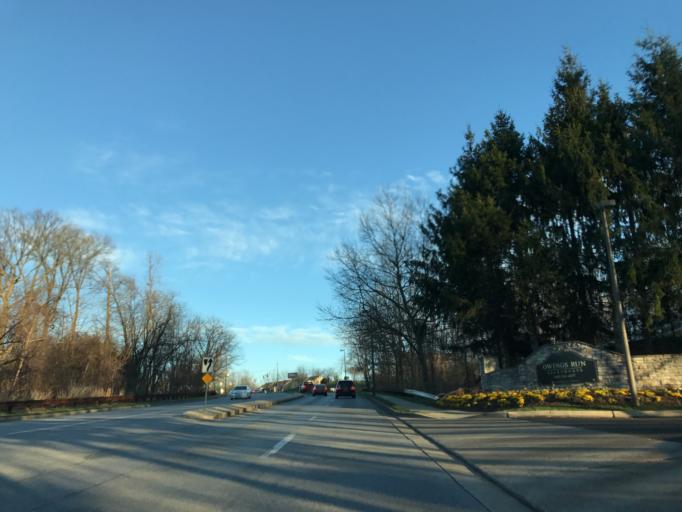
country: US
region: Maryland
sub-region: Baltimore County
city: Owings Mills
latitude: 39.3992
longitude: -76.7984
